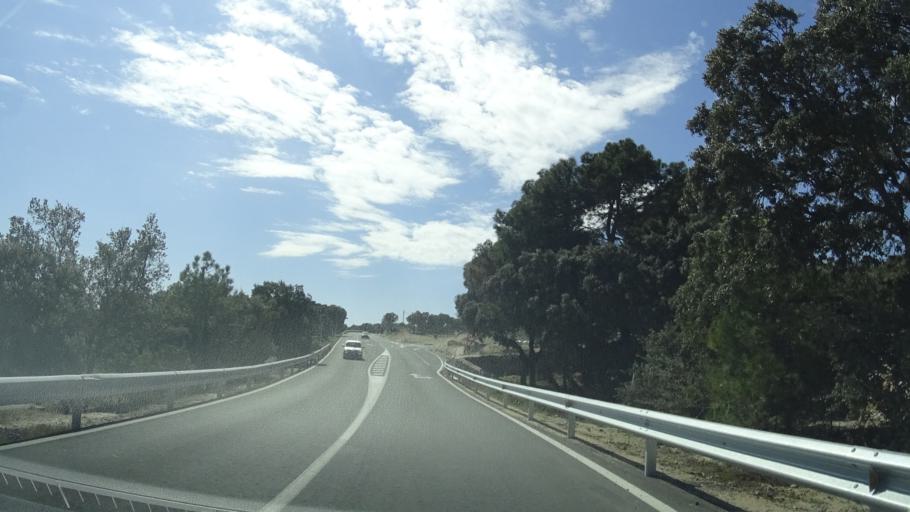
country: ES
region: Madrid
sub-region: Provincia de Madrid
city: Hoyo de Manzanares
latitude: 40.6227
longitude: -3.8864
